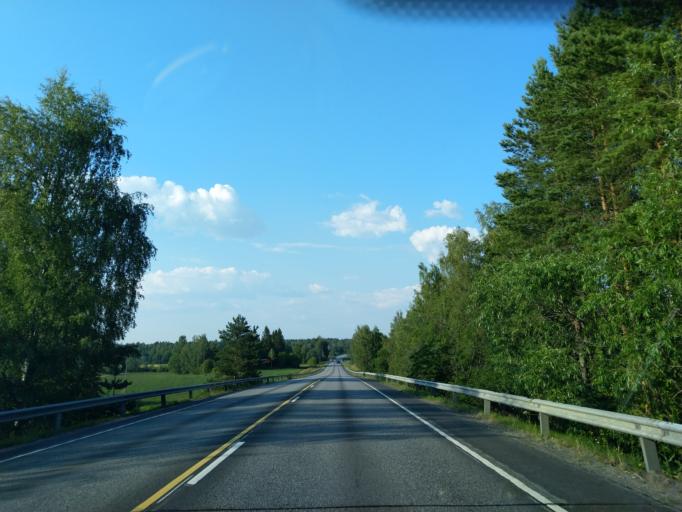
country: FI
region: Satakunta
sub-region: Pori
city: Pomarkku
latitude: 61.6923
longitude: 22.0014
